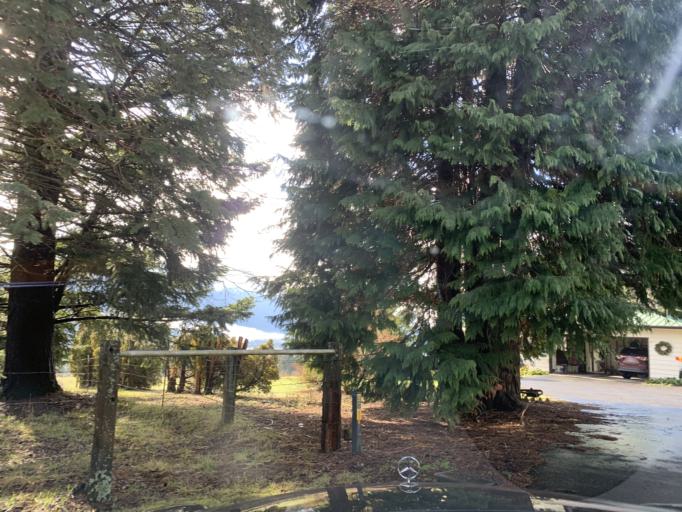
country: US
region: Washington
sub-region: Skamania County
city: Carson
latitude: 45.7222
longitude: -121.8129
